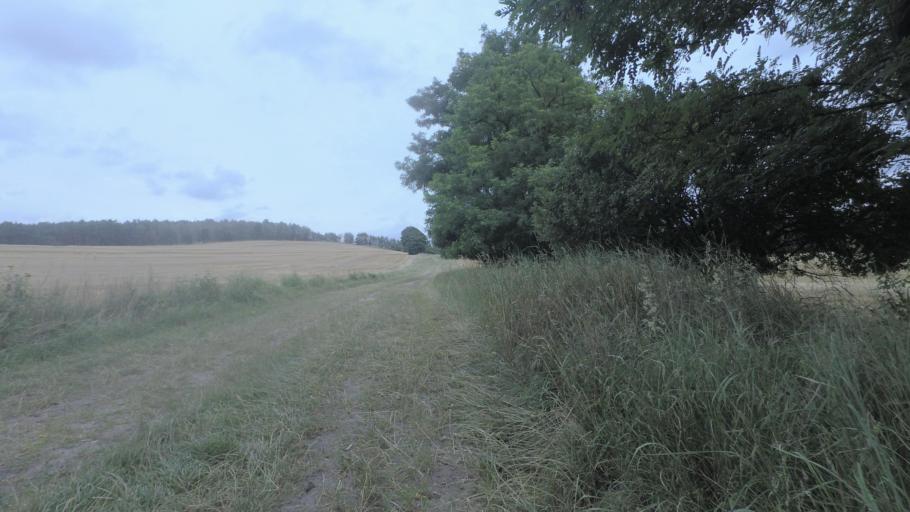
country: DE
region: Brandenburg
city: Rangsdorf
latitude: 52.2638
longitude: 13.3720
